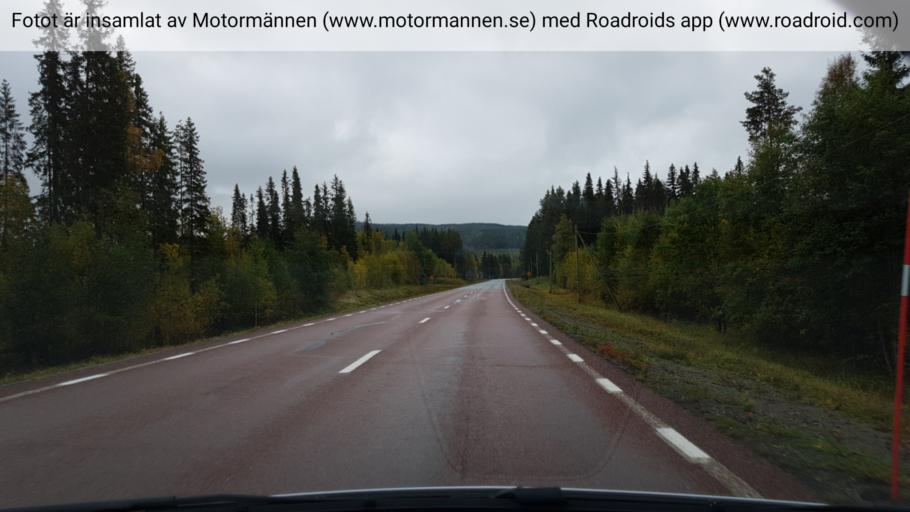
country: SE
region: Vaesterbotten
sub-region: Dorotea Kommun
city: Dorotea
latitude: 64.1910
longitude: 16.3023
